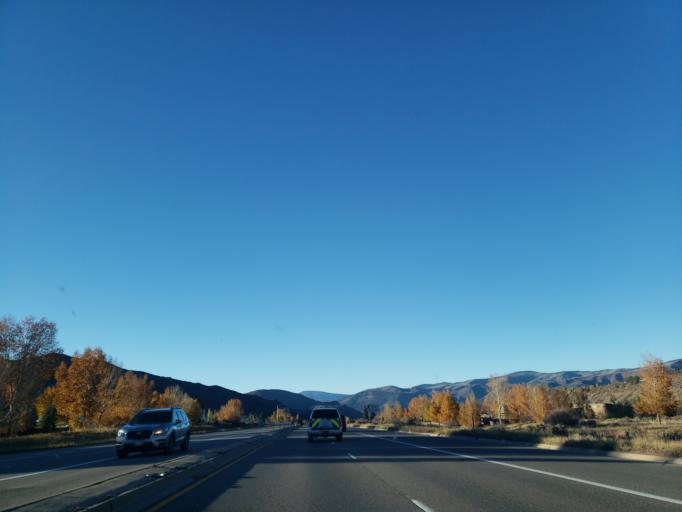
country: US
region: Colorado
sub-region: Pitkin County
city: Aspen
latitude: 39.2211
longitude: -106.8636
